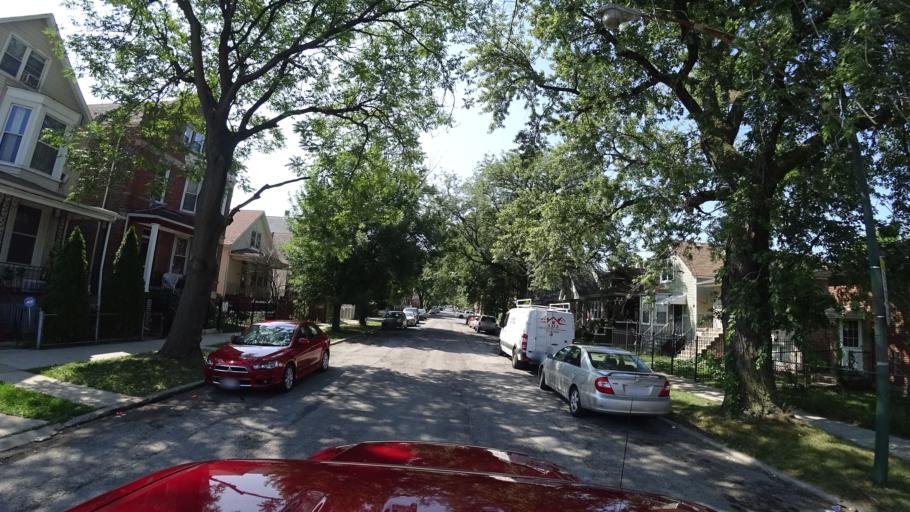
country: US
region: Illinois
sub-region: Cook County
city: Chicago
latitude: 41.8300
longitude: -87.6923
